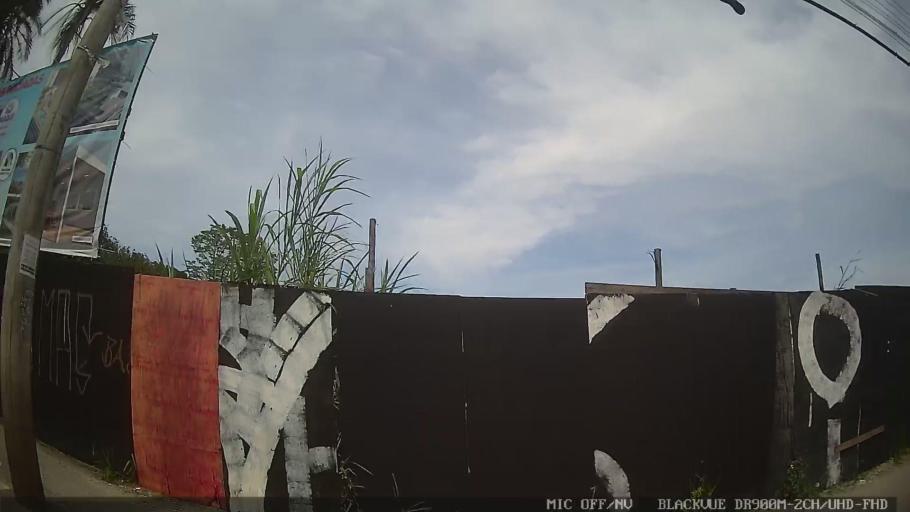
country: BR
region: Sao Paulo
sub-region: Ferraz De Vasconcelos
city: Ferraz de Vasconcelos
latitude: -23.5348
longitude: -46.3665
